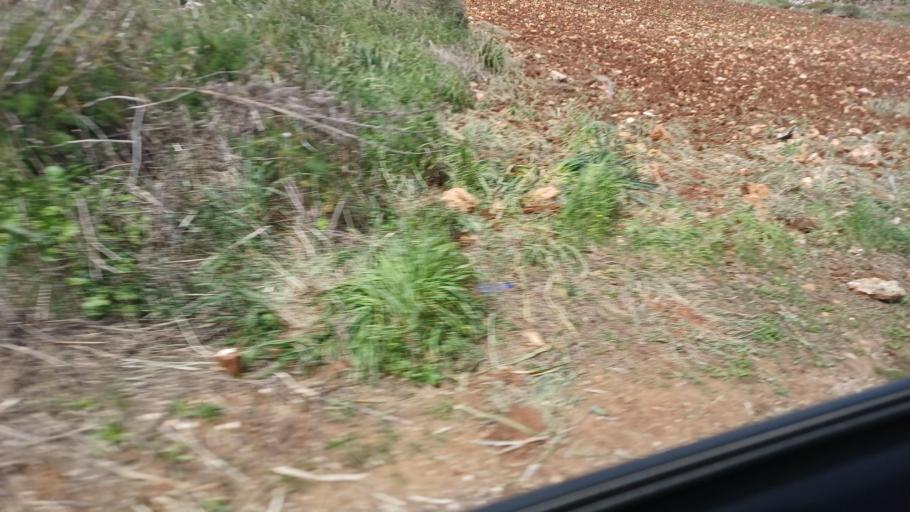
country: CY
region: Pafos
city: Pegeia
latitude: 34.9531
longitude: 32.4031
